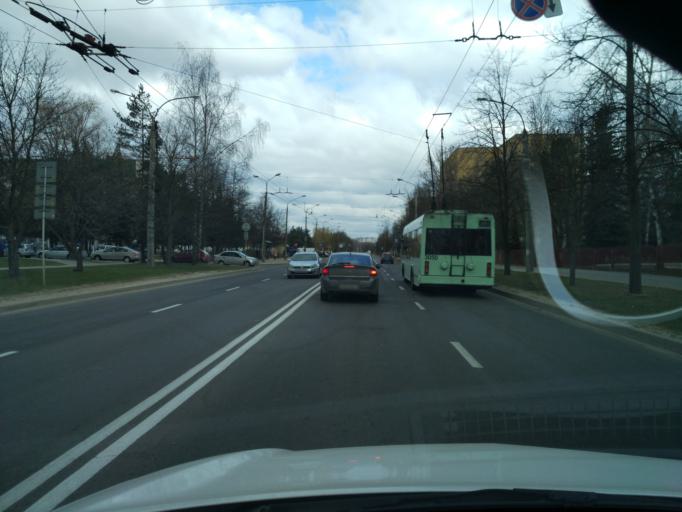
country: BY
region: Minsk
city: Syenitsa
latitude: 53.8589
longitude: 27.4978
